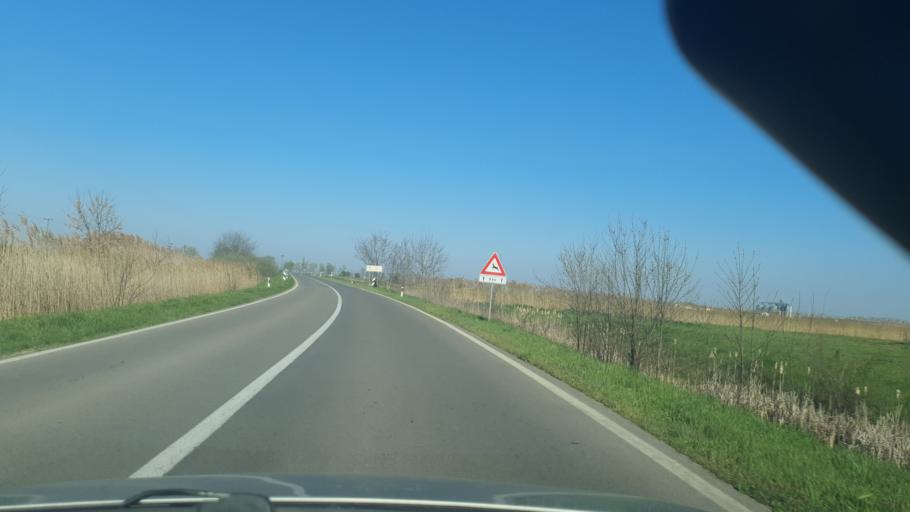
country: RS
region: Autonomna Pokrajina Vojvodina
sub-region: Zapadnobacki Okrug
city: Kula
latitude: 45.7202
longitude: 19.3741
